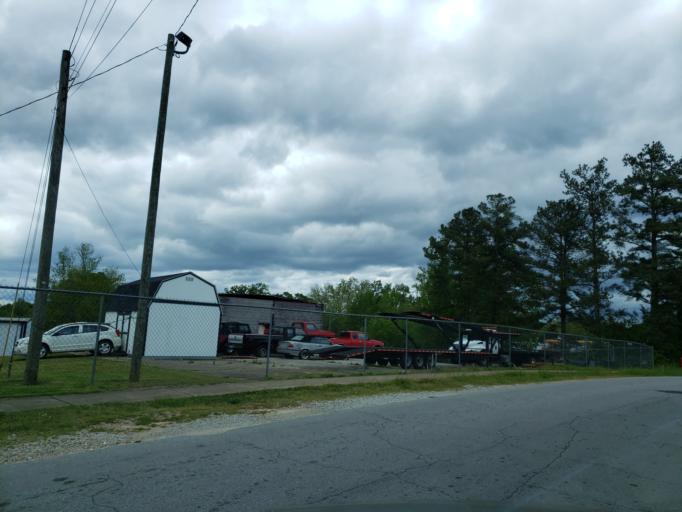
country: US
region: Georgia
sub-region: Haralson County
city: Tallapoosa
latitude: 33.7436
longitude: -85.2921
